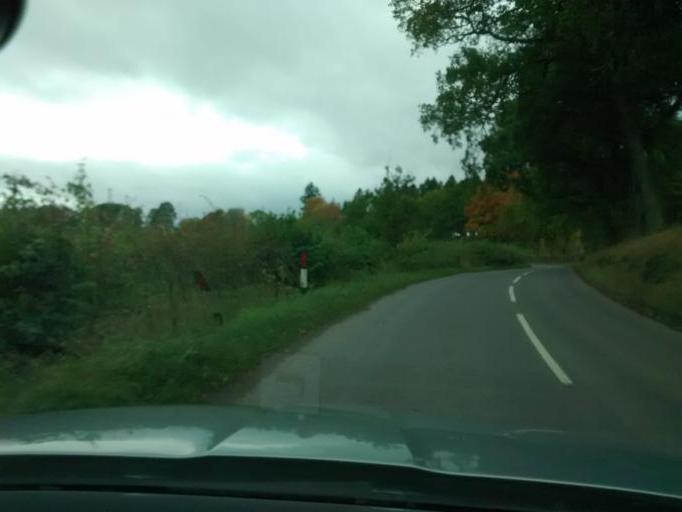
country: GB
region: Scotland
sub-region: Perth and Kinross
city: Stanley
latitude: 56.5191
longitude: -3.3963
